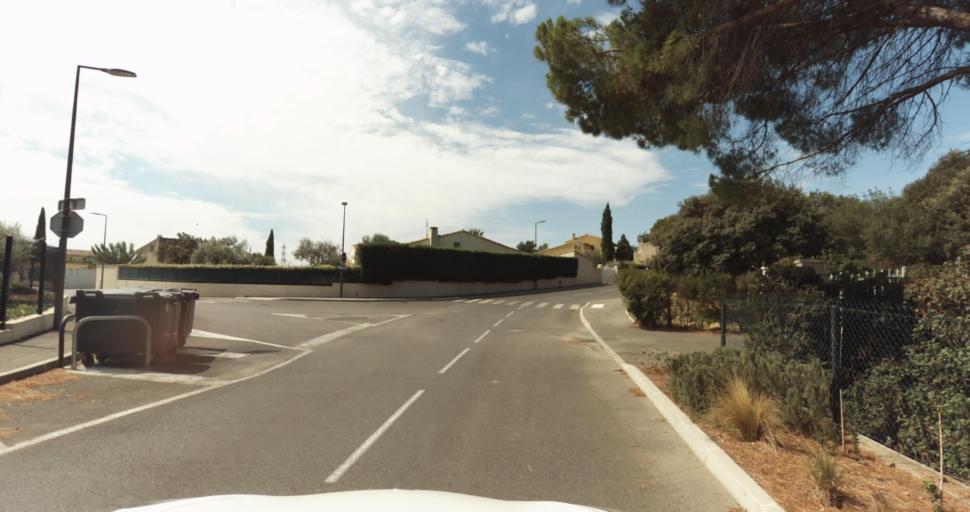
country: FR
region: Provence-Alpes-Cote d'Azur
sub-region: Departement des Bouches-du-Rhone
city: Miramas
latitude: 43.5795
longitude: 5.0253
